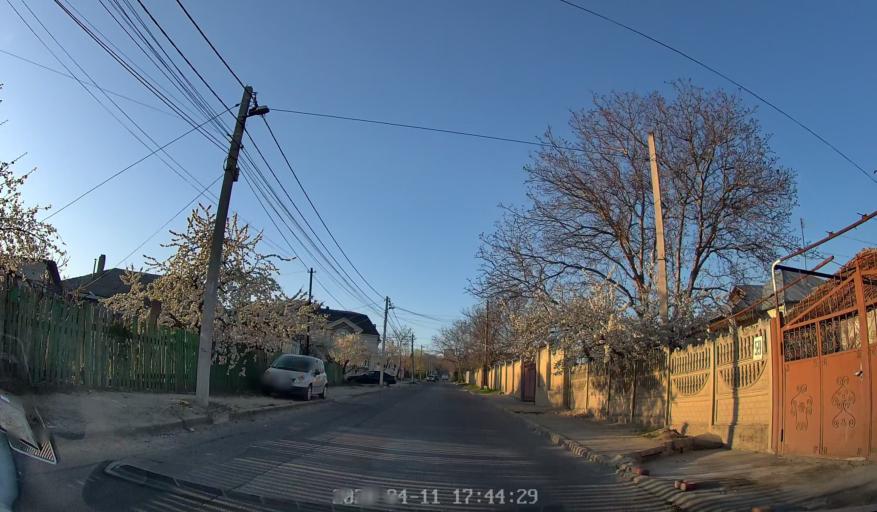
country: MD
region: Chisinau
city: Chisinau
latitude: 46.9782
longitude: 28.8239
